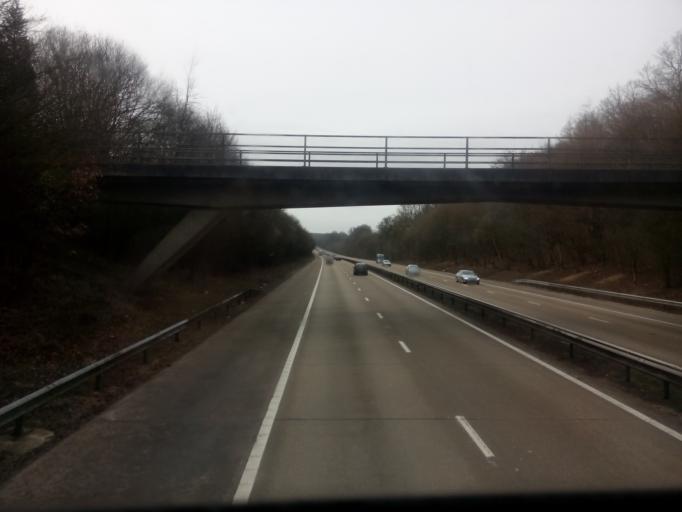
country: GB
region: England
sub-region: Hampshire
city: Overton
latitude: 51.1653
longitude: -1.2301
